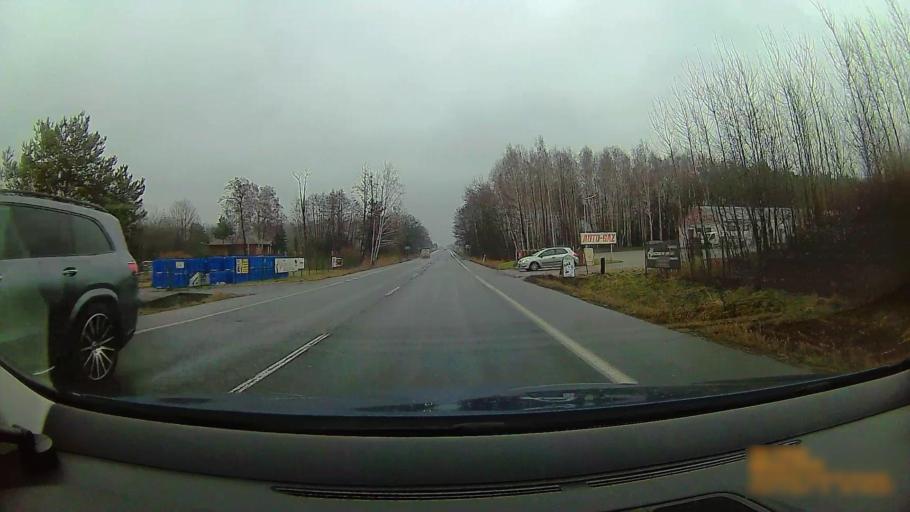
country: PL
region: Greater Poland Voivodeship
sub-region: Powiat koninski
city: Stare Miasto
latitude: 52.1895
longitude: 18.2330
